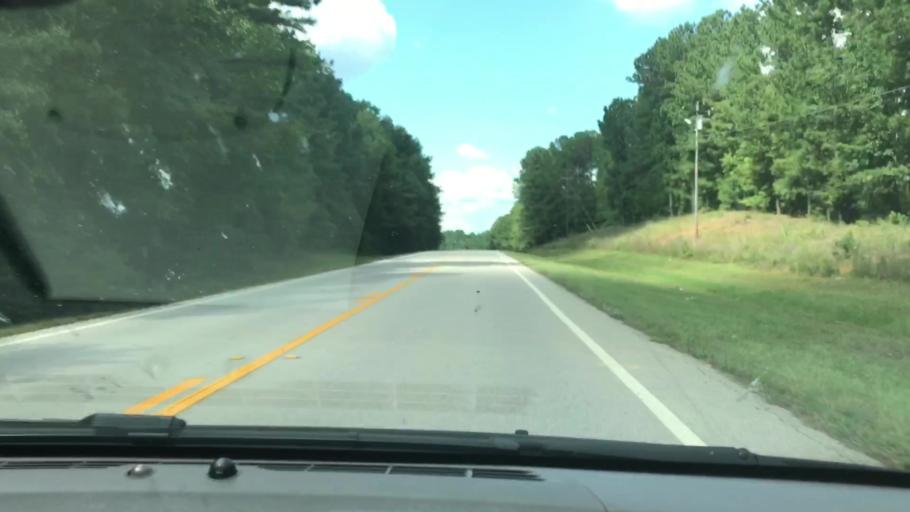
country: US
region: Georgia
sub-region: Troup County
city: La Grange
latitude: 33.0912
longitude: -85.0579
